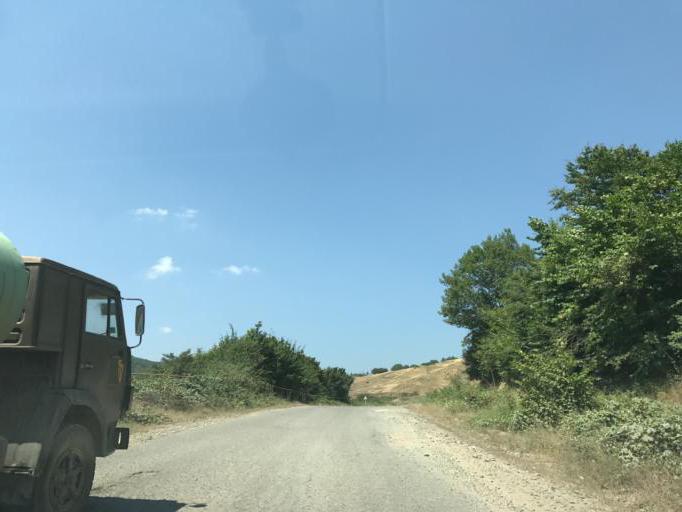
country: AZ
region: Tartar Rayon
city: Martakert
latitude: 40.1038
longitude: 46.6527
